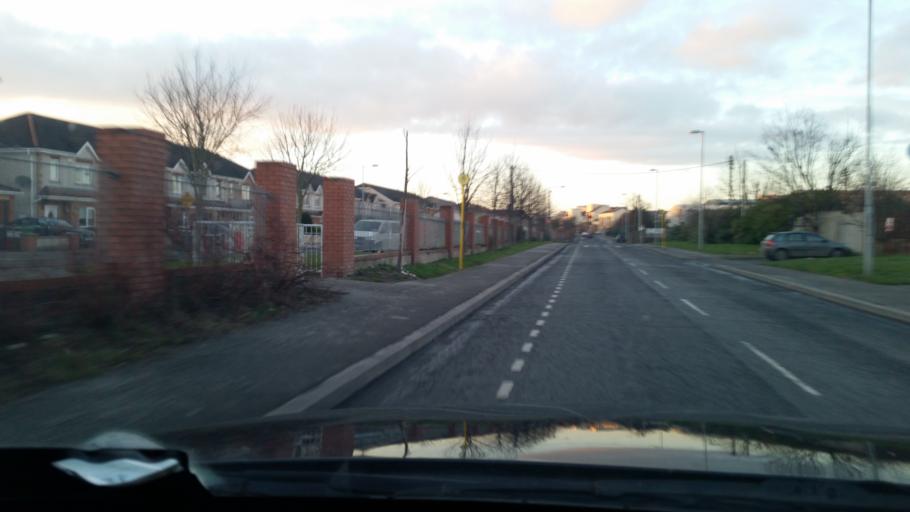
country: IE
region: Leinster
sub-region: Dublin City
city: Finglas
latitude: 53.4018
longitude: -6.2916
